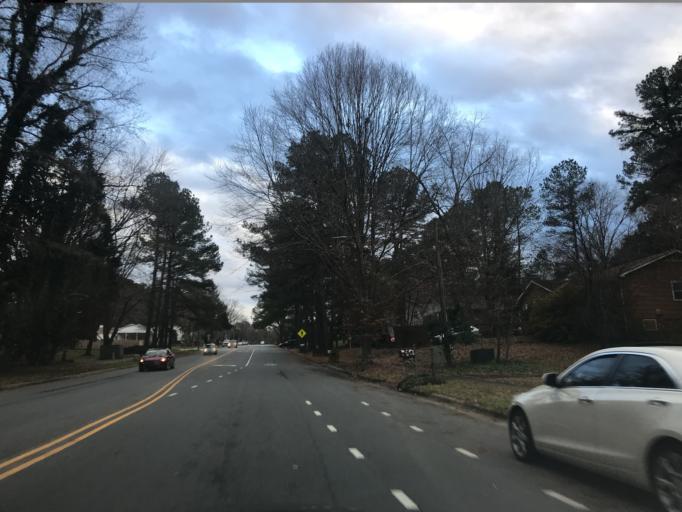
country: US
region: North Carolina
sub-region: Wake County
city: West Raleigh
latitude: 35.8641
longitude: -78.6541
